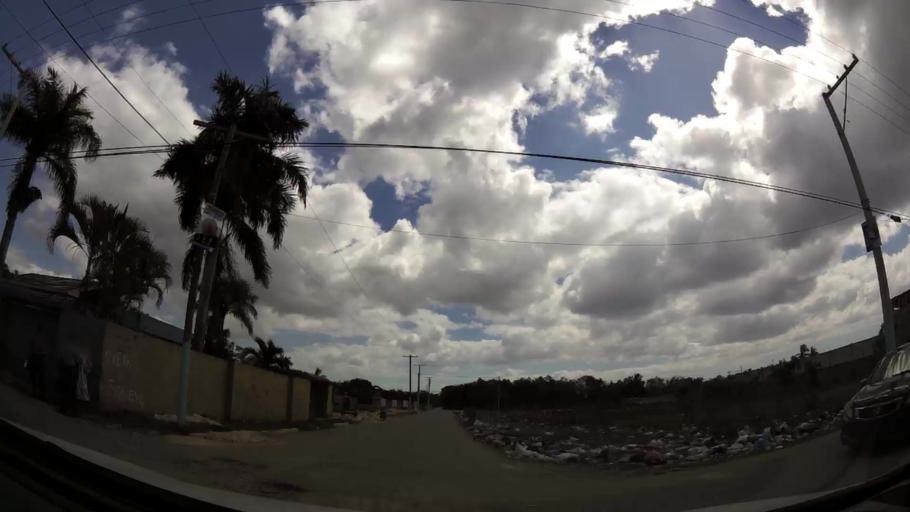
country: DO
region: Santo Domingo
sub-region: Santo Domingo
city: Boca Chica
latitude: 18.4531
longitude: -69.6422
